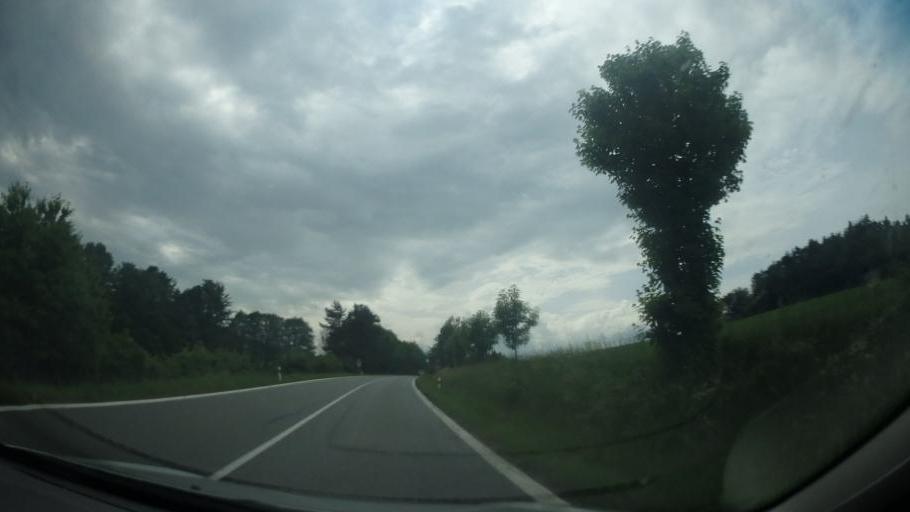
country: CZ
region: Vysocina
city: Bystrice nad Pernstejnem
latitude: 49.5203
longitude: 16.3001
